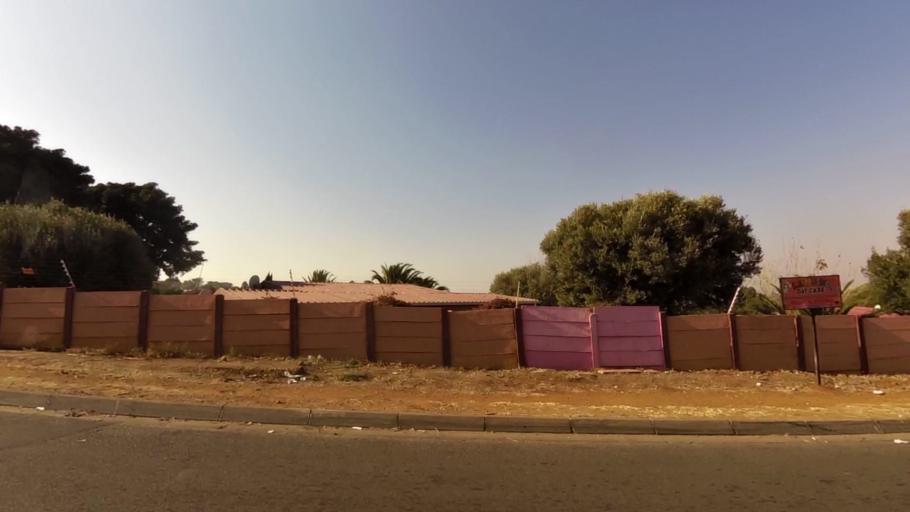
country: ZA
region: Gauteng
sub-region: City of Johannesburg Metropolitan Municipality
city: Soweto
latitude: -26.2908
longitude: 27.9521
